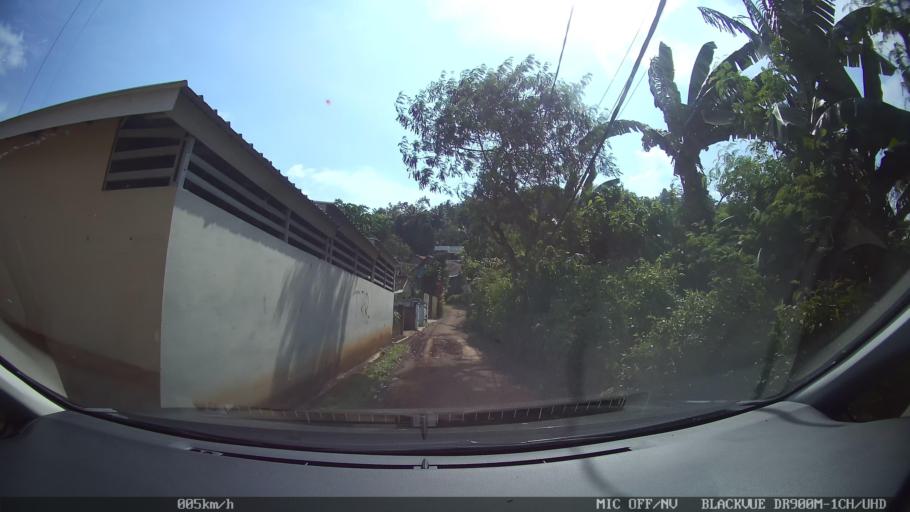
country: ID
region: Lampung
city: Kedaton
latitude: -5.3966
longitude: 105.2287
